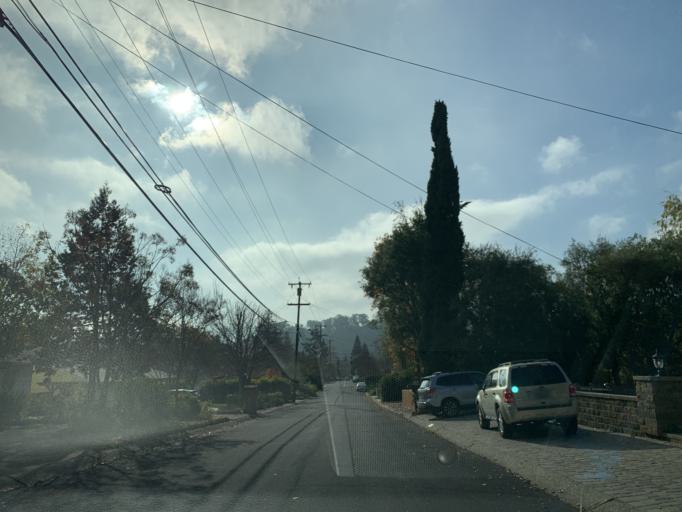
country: US
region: California
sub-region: Contra Costa County
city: Saranap
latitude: 37.8918
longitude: -122.0813
